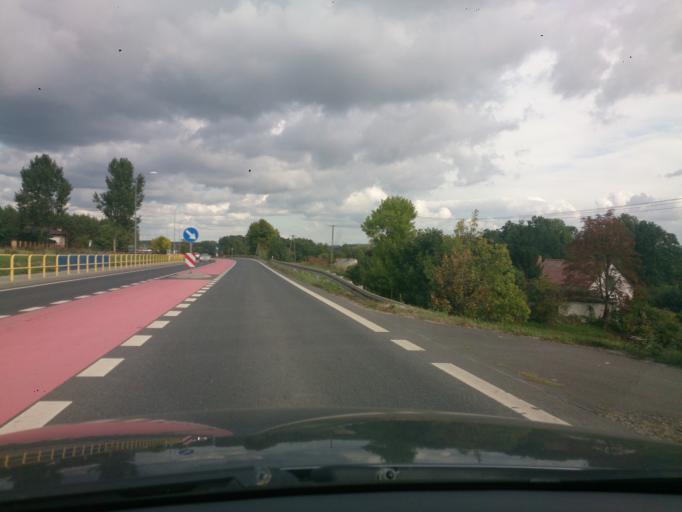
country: PL
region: Kujawsko-Pomorskie
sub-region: Grudziadz
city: Grudziadz
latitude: 53.4895
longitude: 18.6771
